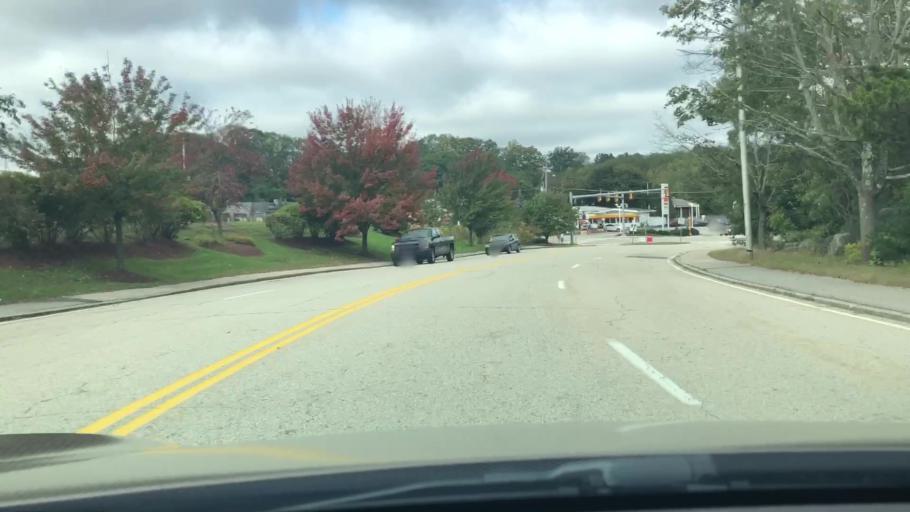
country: US
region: Massachusetts
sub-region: Worcester County
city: Auburn
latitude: 42.2037
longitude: -71.8352
